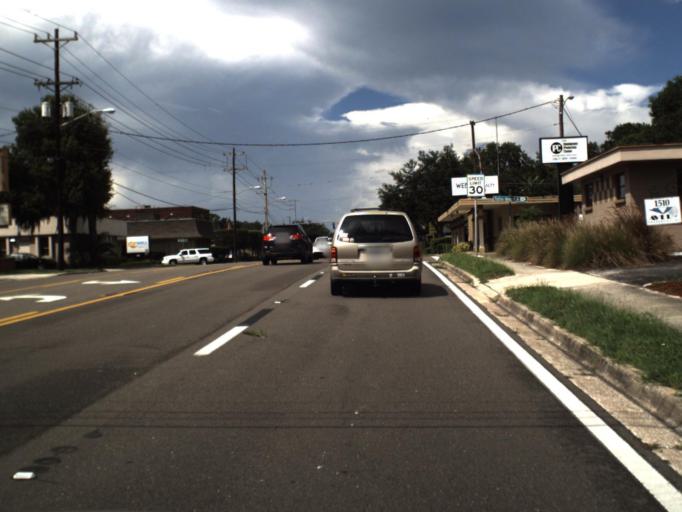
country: US
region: Florida
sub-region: Polk County
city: Lakeland
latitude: 28.0241
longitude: -81.9570
